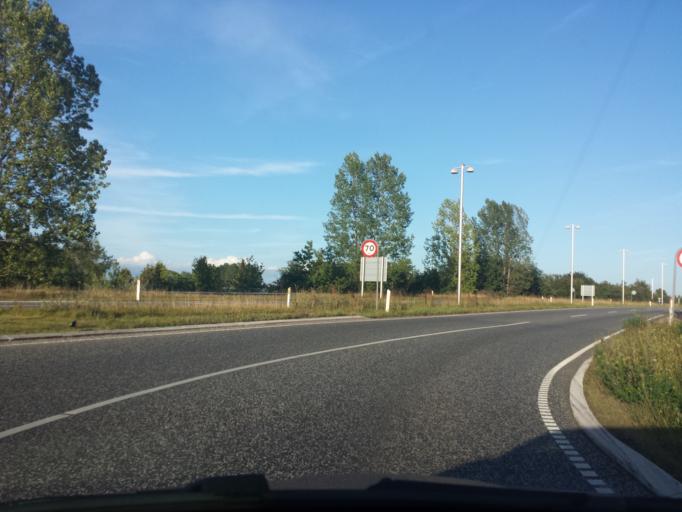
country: DK
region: Capital Region
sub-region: Egedal Kommune
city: Olstykke
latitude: 55.7845
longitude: 12.1522
